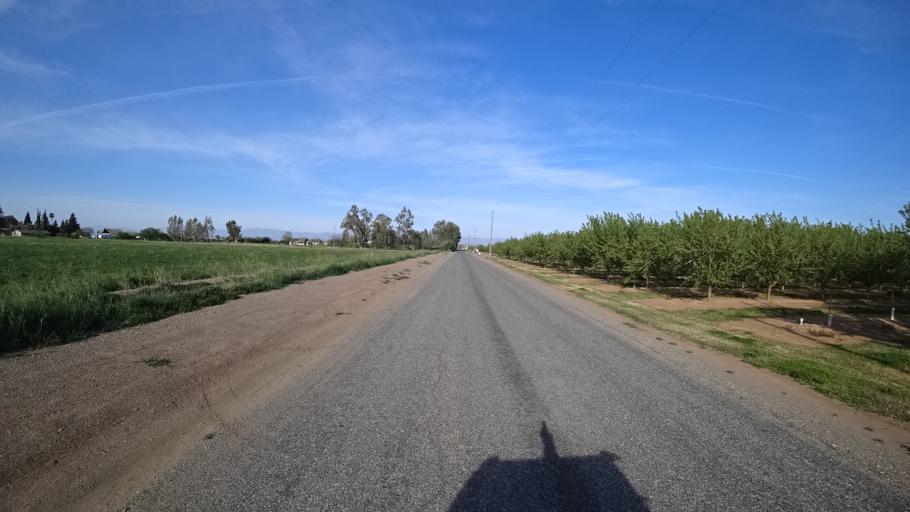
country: US
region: California
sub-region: Glenn County
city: Orland
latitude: 39.7187
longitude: -122.2235
